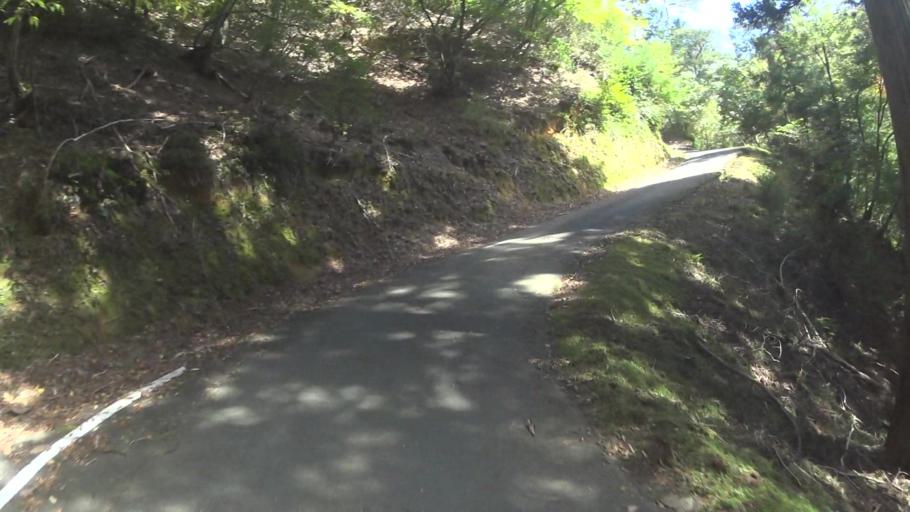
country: JP
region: Hyogo
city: Toyooka
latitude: 35.6060
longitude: 134.9957
